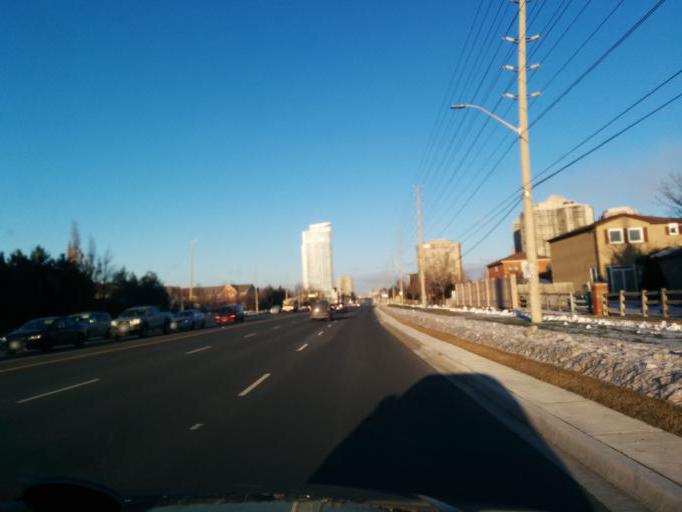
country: CA
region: Ontario
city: Mississauga
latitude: 43.6004
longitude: -79.6599
